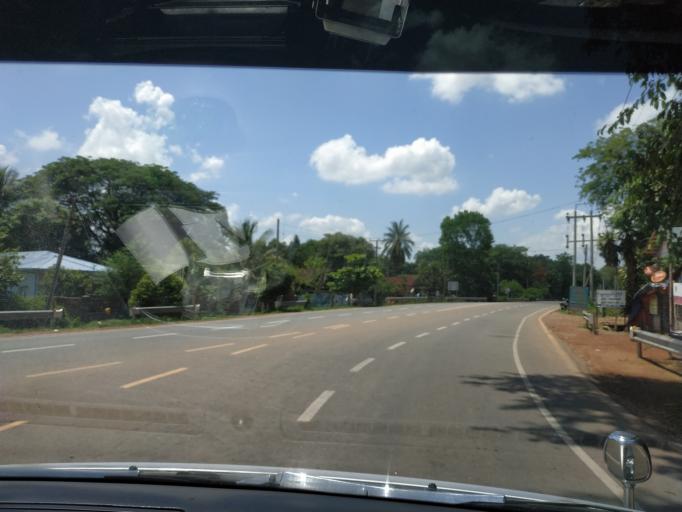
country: MM
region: Mon
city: Kyaikto
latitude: 17.3146
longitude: 97.0186
